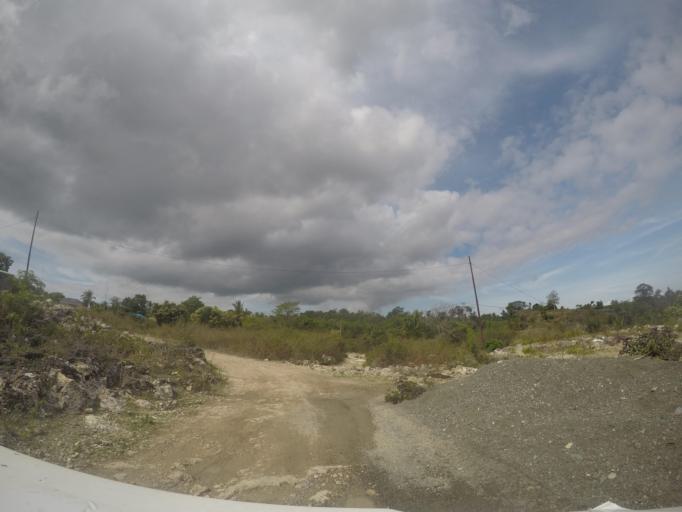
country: TL
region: Baucau
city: Baucau
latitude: -8.4681
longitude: 126.4575
